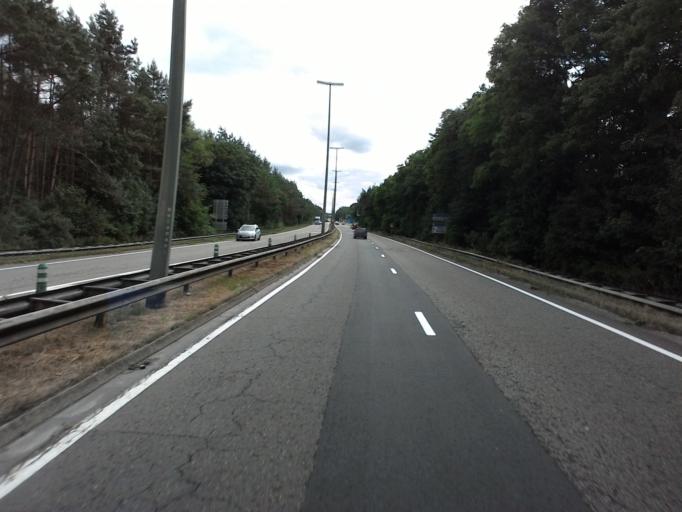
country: BE
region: Wallonia
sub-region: Province du Luxembourg
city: Arlon
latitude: 49.6761
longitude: 5.7798
